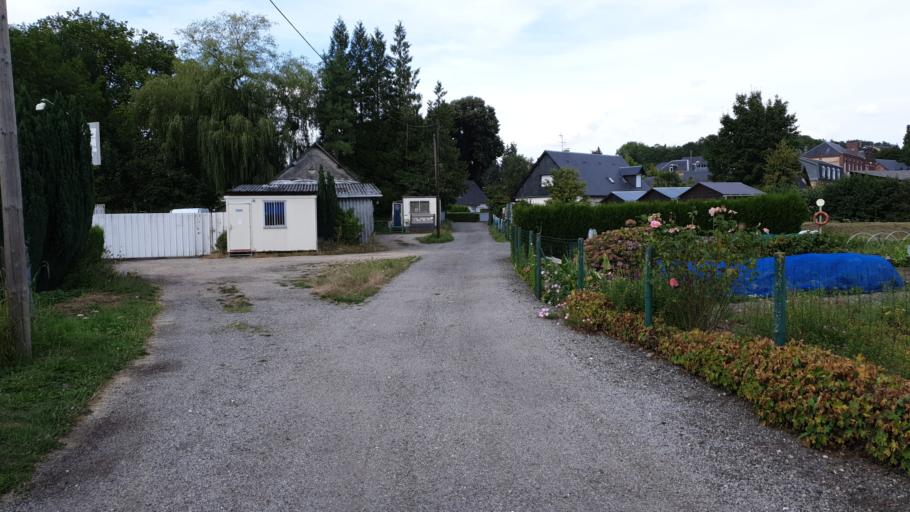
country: FR
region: Haute-Normandie
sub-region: Departement de la Seine-Maritime
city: Lillebonne
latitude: 49.5156
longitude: 0.5338
